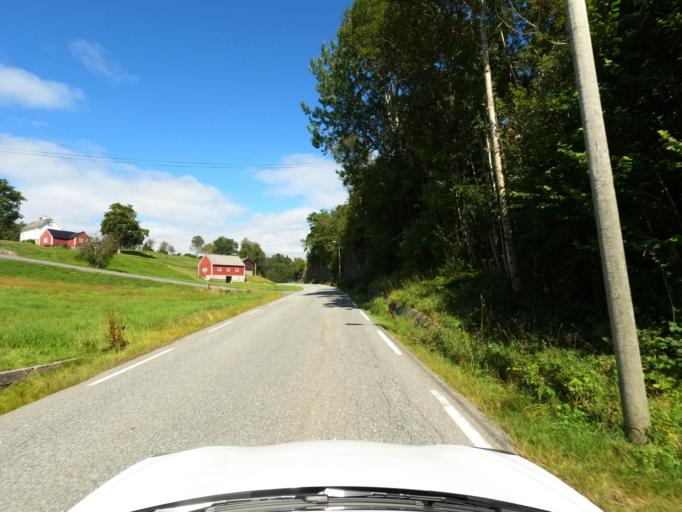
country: NO
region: Hordaland
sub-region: Os
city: Hagavik
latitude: 60.1648
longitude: 5.3411
